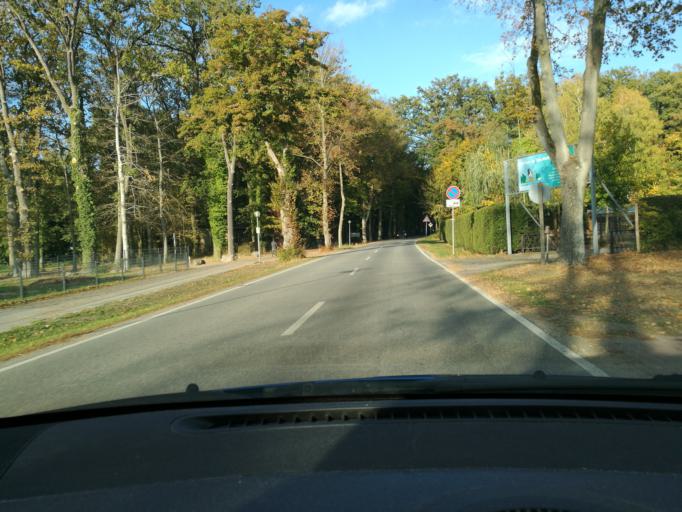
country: DE
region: Saxony-Anhalt
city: Luftkurort Arendsee
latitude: 52.8867
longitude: 11.4981
